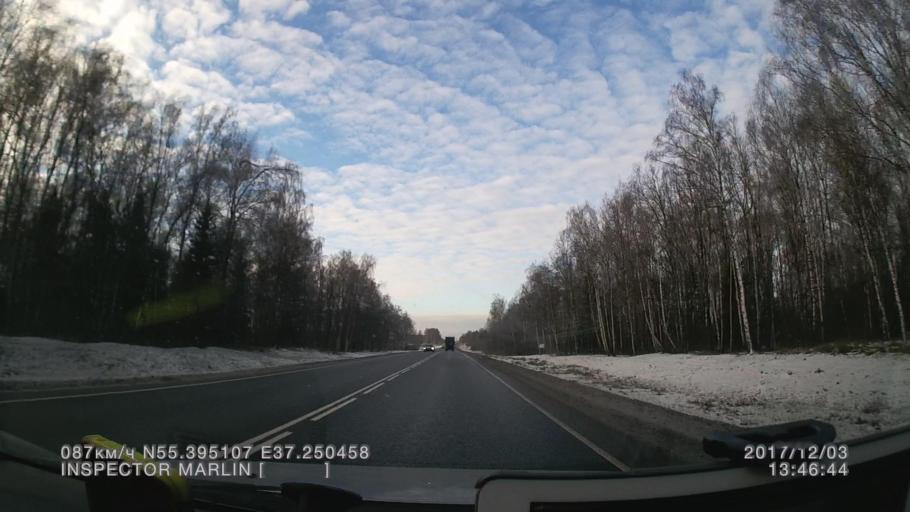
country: RU
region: Moskovskaya
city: Troitsk
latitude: 55.3950
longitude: 37.2509
